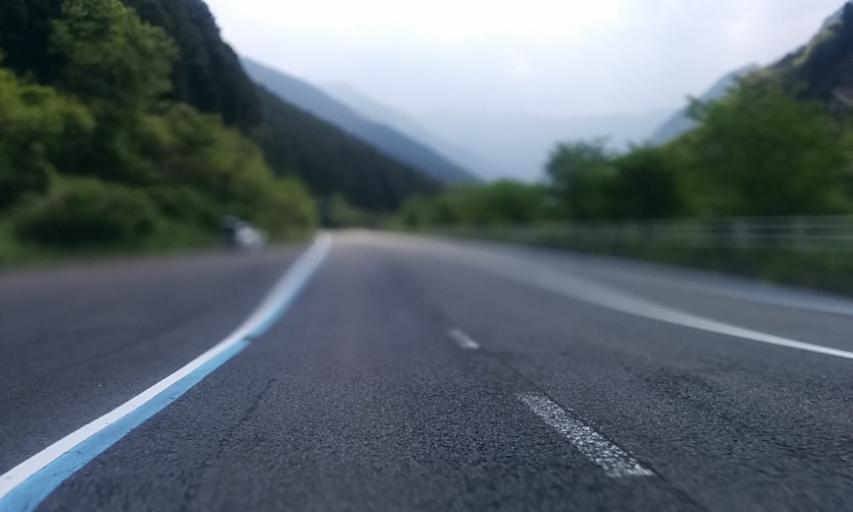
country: JP
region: Ehime
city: Saijo
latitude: 33.8277
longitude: 133.2332
